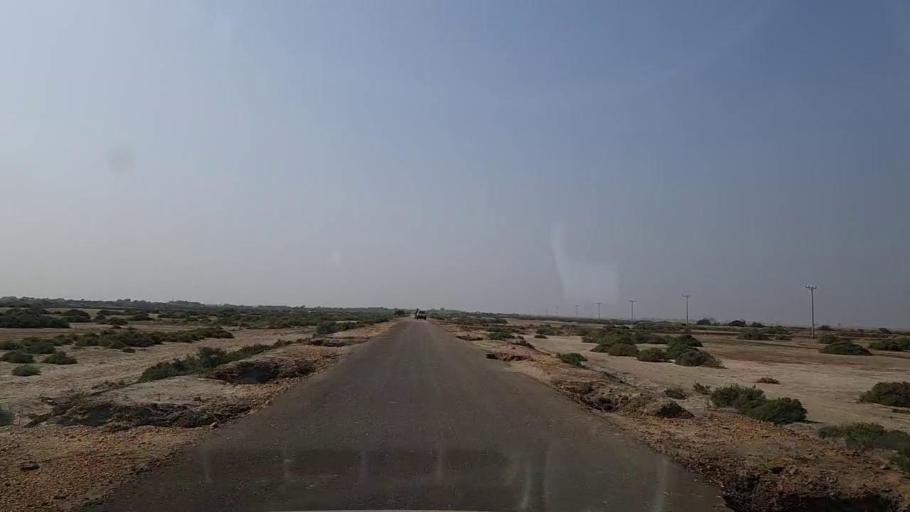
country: PK
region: Sindh
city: Mirpur Sakro
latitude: 24.5288
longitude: 67.5722
